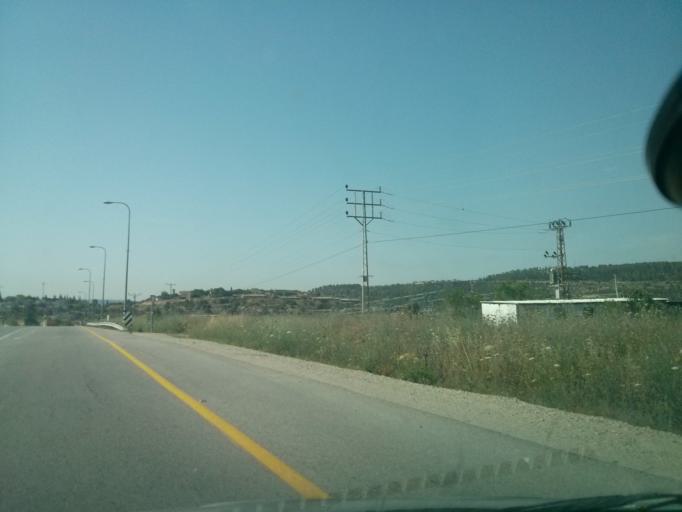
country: IL
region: Jerusalem
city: Bet Shemesh
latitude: 31.6827
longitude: 35.0026
